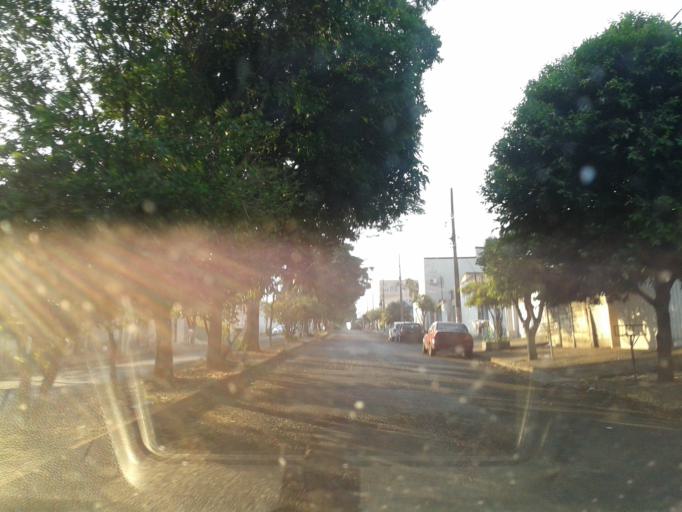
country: BR
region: Minas Gerais
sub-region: Uberlandia
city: Uberlandia
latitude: -18.9065
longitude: -48.2421
